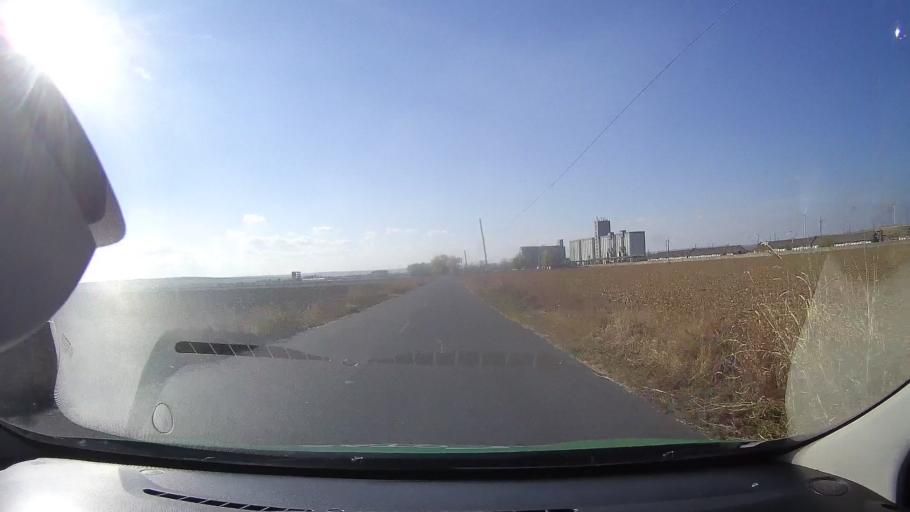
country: RO
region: Tulcea
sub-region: Comuna Ceamurlia de Jos
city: Ceamurlia de Jos
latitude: 44.7391
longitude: 28.6920
